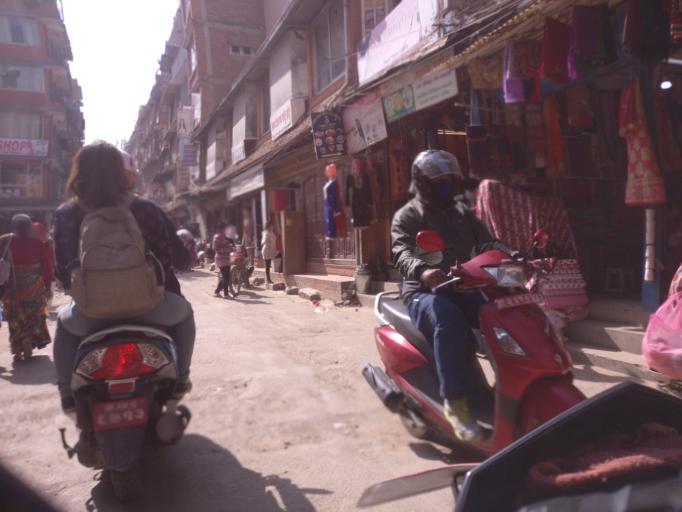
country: NP
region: Central Region
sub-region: Bagmati Zone
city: Patan
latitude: 27.6706
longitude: 85.3239
